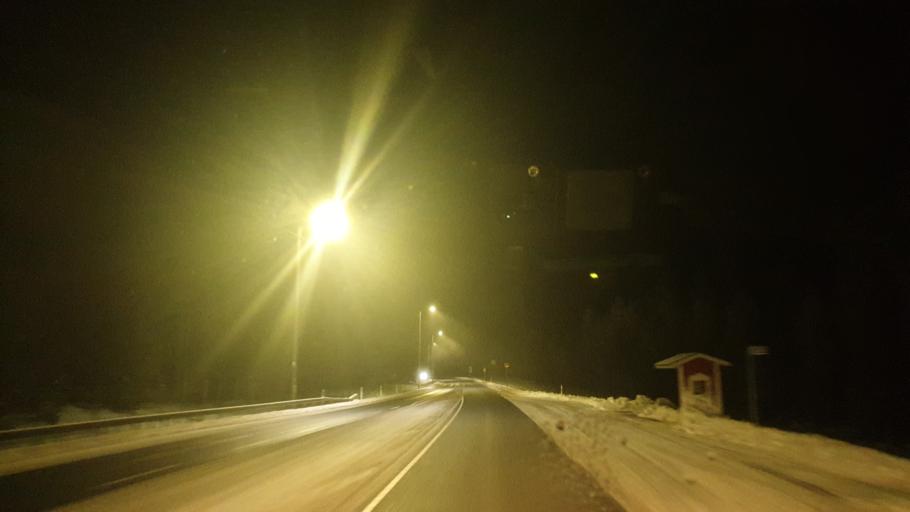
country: FI
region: Northern Ostrobothnia
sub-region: Oulunkaari
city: Kuivaniemi
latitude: 65.5391
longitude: 25.2453
